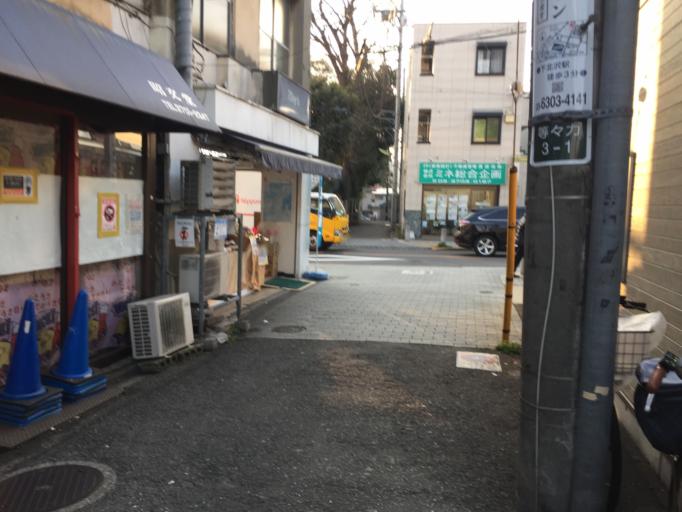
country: JP
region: Tokyo
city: Tokyo
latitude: 35.6085
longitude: 139.6474
